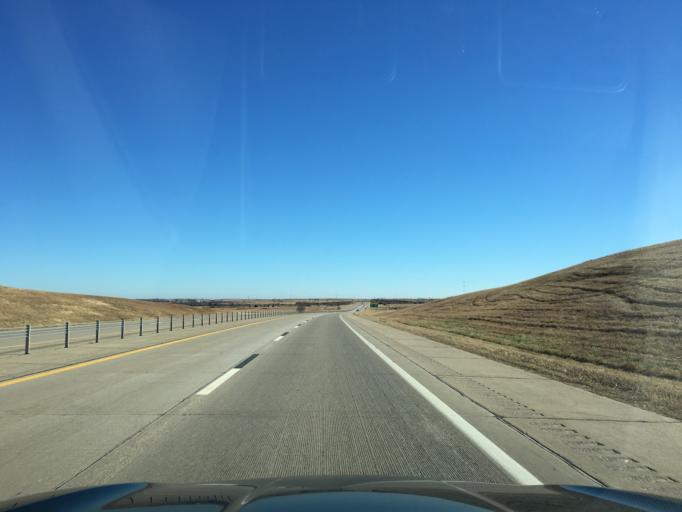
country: US
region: Oklahoma
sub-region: Noble County
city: Perry
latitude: 36.3909
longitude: -97.1008
